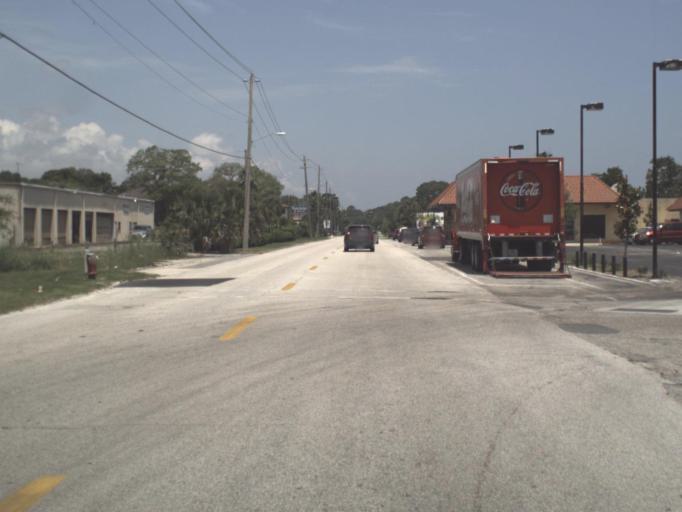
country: US
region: Florida
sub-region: Saint Johns County
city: Saint Augustine
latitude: 29.9181
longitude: -81.3230
